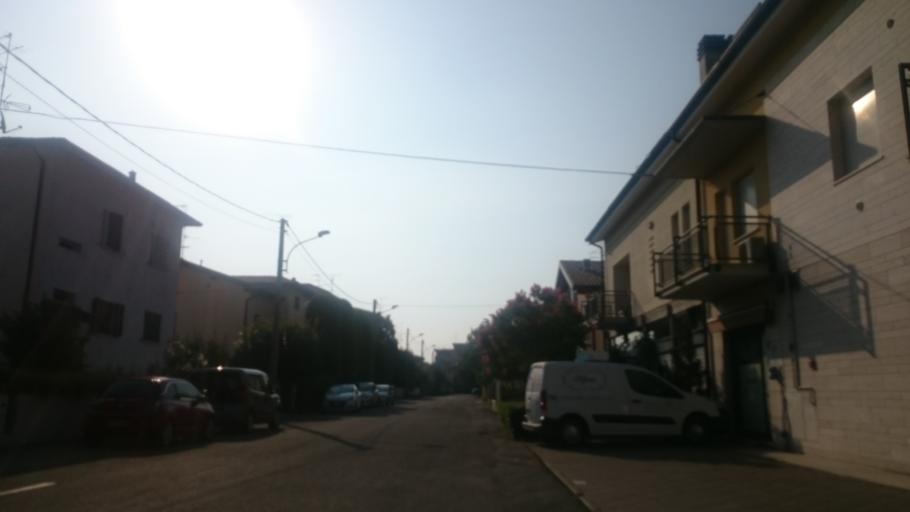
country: IT
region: Emilia-Romagna
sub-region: Provincia di Reggio Emilia
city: Scandiano
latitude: 44.5974
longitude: 10.6917
